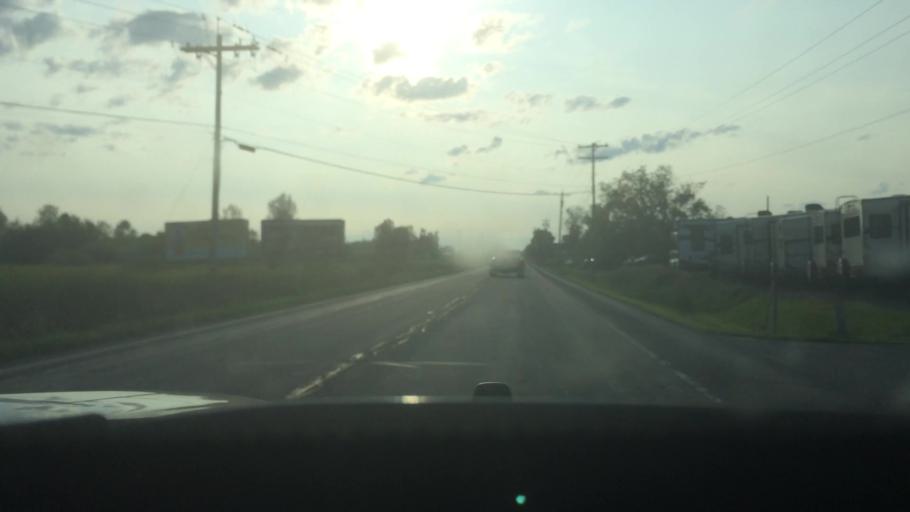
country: US
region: New York
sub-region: St. Lawrence County
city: Ogdensburg
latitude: 44.6887
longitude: -75.4643
